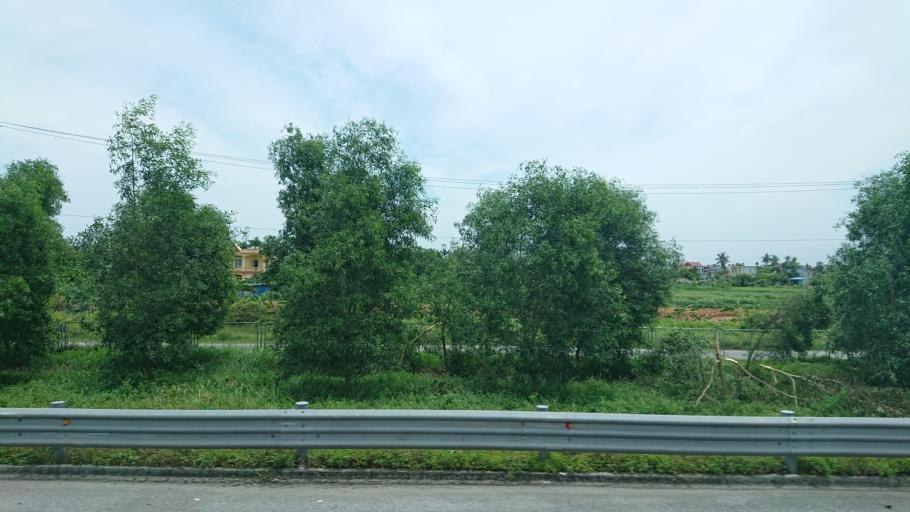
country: VN
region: Hai Phong
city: Nui Doi
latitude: 20.7692
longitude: 106.6294
